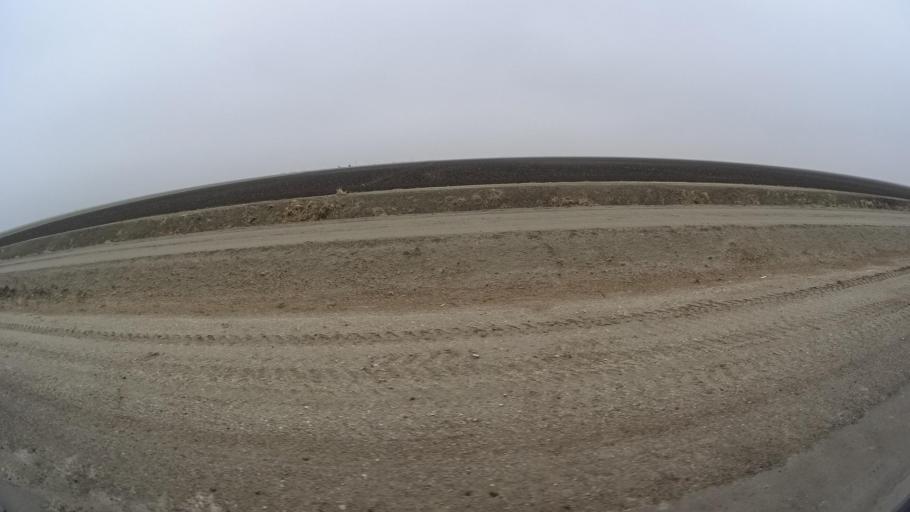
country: US
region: California
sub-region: Kern County
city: Rosedale
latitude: 35.1944
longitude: -119.2186
